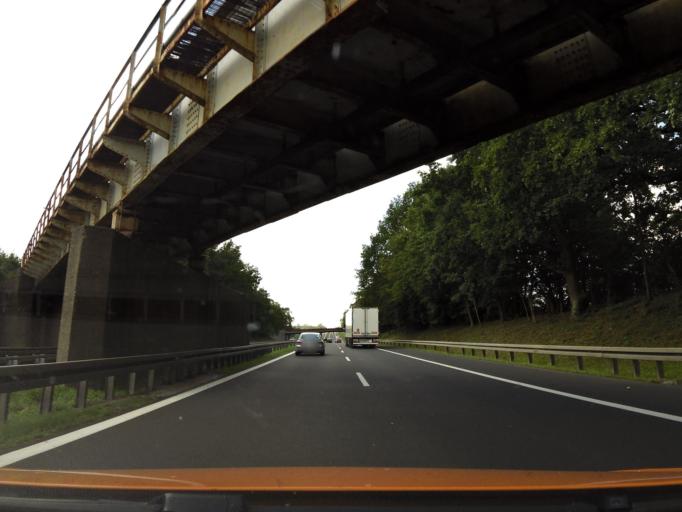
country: PL
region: West Pomeranian Voivodeship
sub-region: Powiat policki
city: Kolbaskowo
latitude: 53.3394
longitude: 14.4349
